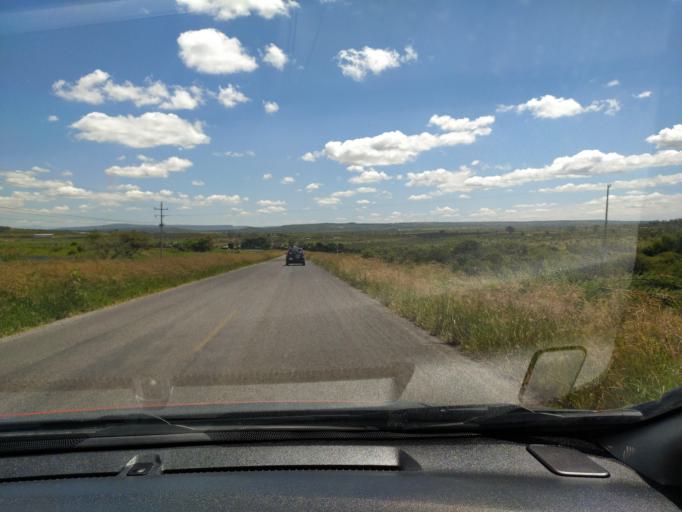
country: MX
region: Jalisco
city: San Julian
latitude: 21.0024
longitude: -102.1049
